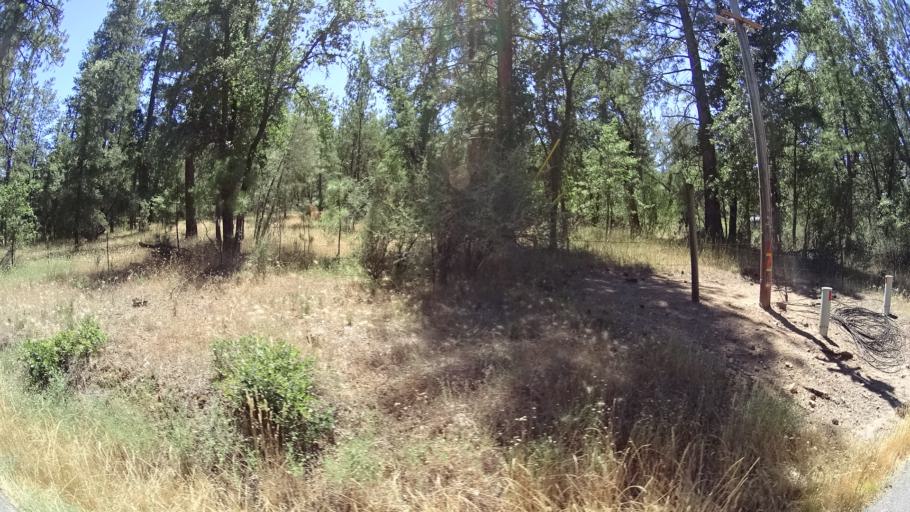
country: US
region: California
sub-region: Calaveras County
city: Mountain Ranch
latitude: 38.2634
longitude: -120.4874
